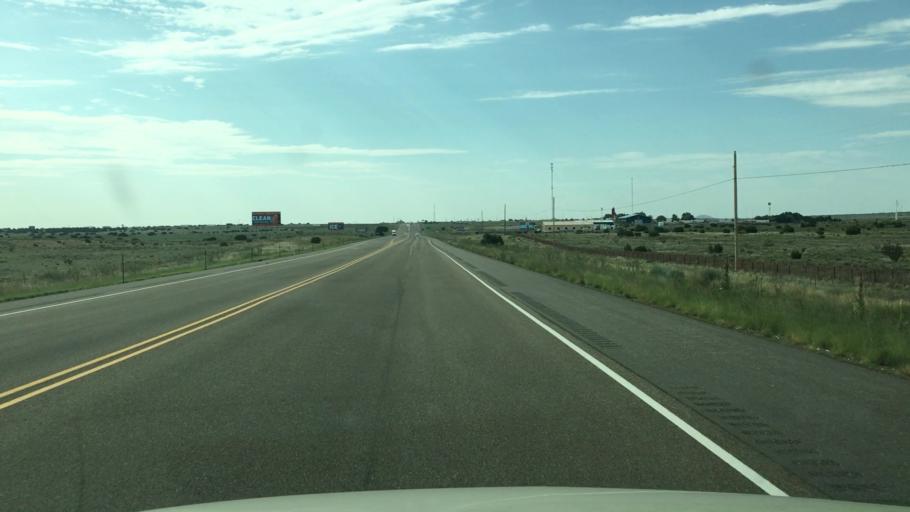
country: US
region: New Mexico
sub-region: Torrance County
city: Moriarty
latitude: 35.0206
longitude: -105.6712
